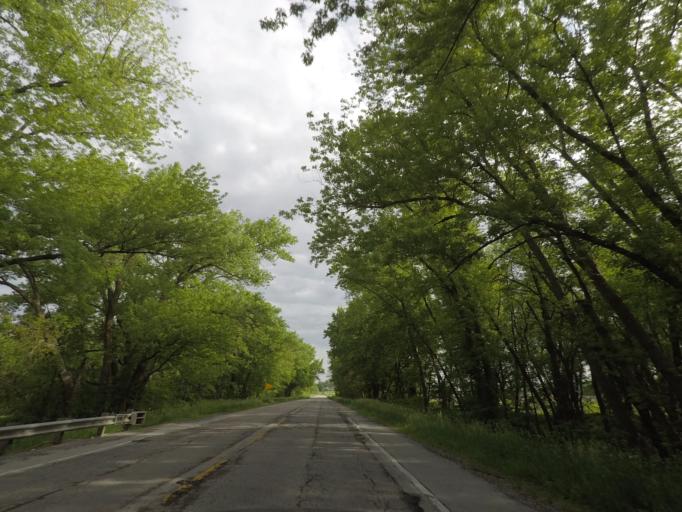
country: US
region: Illinois
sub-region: Logan County
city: Mount Pulaski
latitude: 40.0548
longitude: -89.2820
